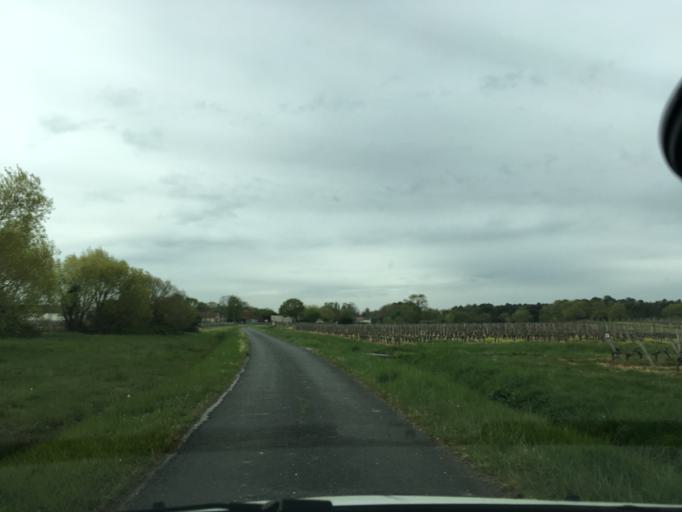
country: FR
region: Aquitaine
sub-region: Departement de la Gironde
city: Lesparre-Medoc
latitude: 45.3167
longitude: -0.8951
